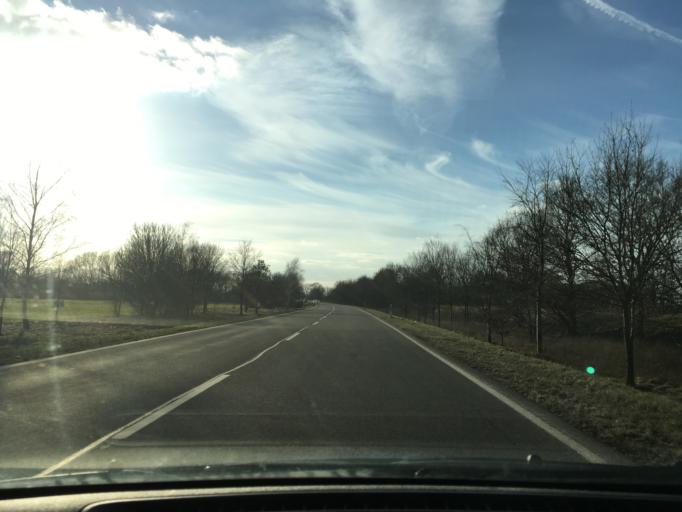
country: DE
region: Saxony-Anhalt
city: Luftkurort Arendsee
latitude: 52.8794
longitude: 11.5179
